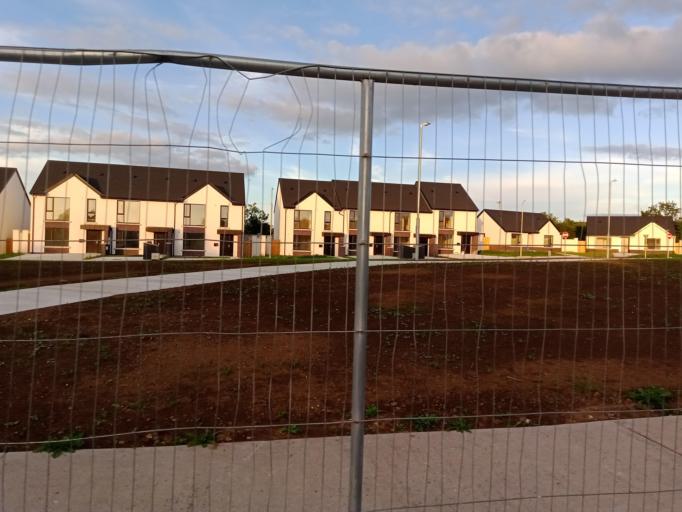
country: IE
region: Leinster
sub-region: Laois
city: Abbeyleix
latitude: 52.8403
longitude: -7.4033
